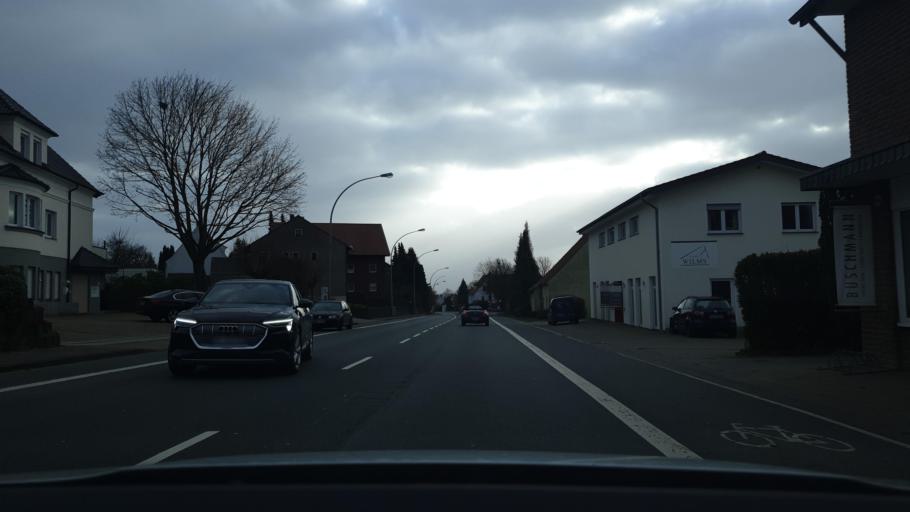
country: DE
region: North Rhine-Westphalia
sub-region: Regierungsbezirk Detmold
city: Huellhorst
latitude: 52.2687
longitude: 8.6355
